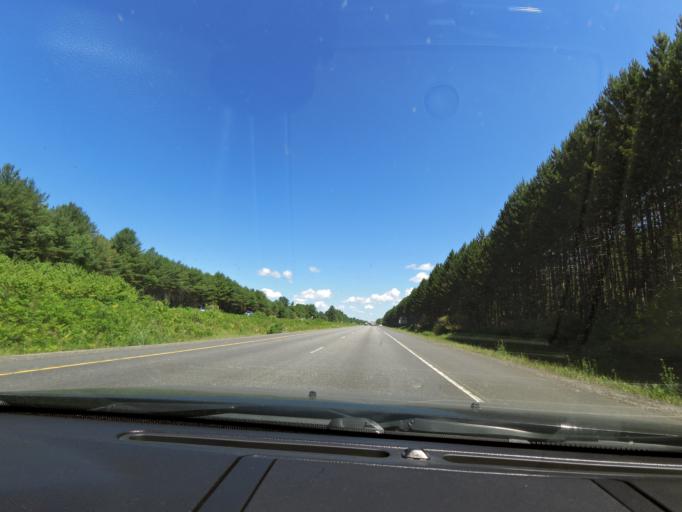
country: CA
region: Ontario
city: Bracebridge
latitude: 45.1225
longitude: -79.3107
